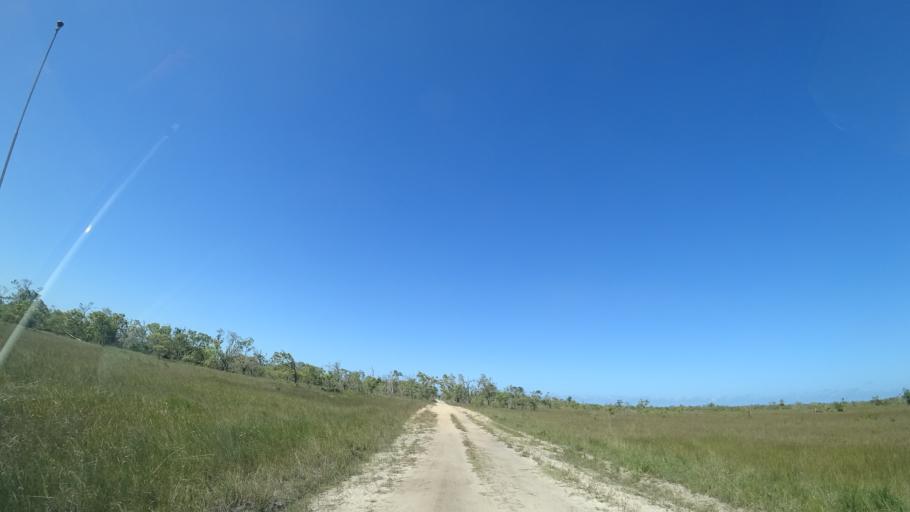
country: MZ
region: Sofala
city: Beira
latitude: -19.5756
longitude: 35.2082
